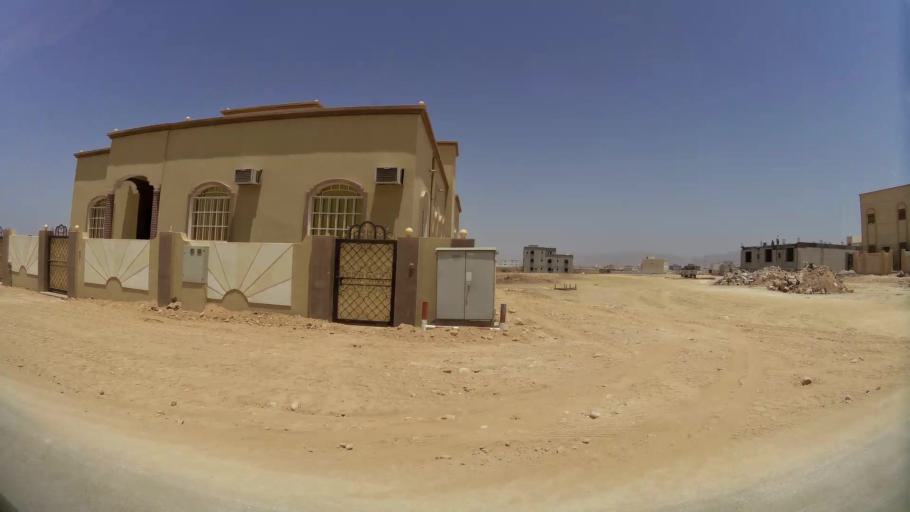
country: OM
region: Zufar
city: Salalah
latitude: 17.0989
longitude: 54.2055
